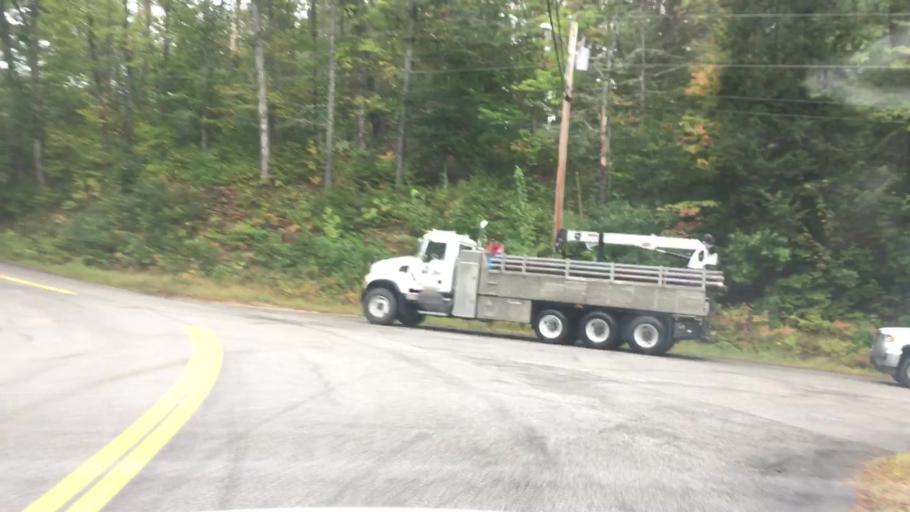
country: US
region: Maine
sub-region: Cumberland County
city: Raymond
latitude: 43.9981
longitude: -70.5723
